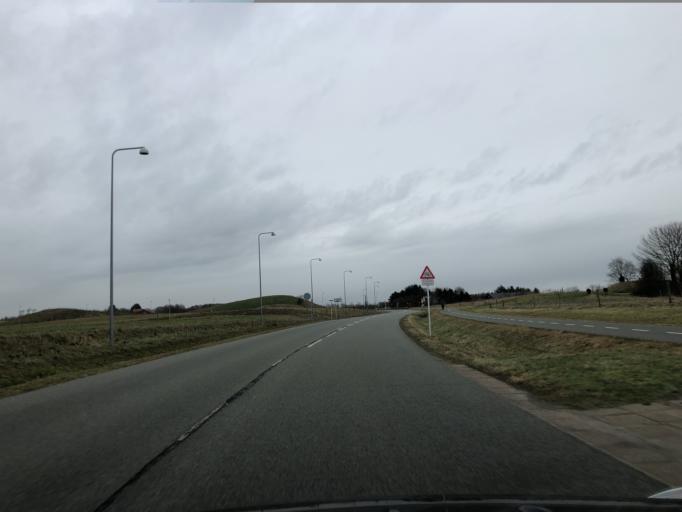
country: DK
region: Central Jutland
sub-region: Holstebro Kommune
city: Holstebro
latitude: 56.3613
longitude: 8.6721
